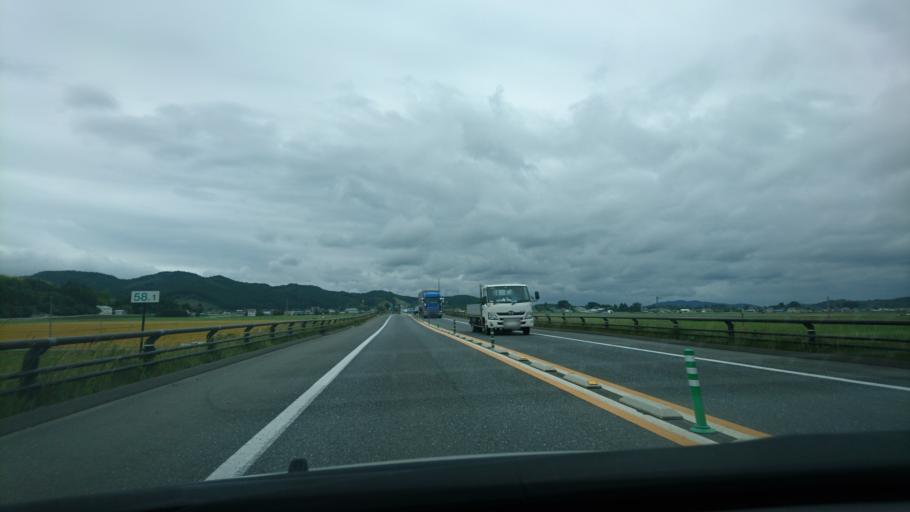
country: JP
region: Miyagi
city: Wakuya
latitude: 38.6168
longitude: 141.2850
